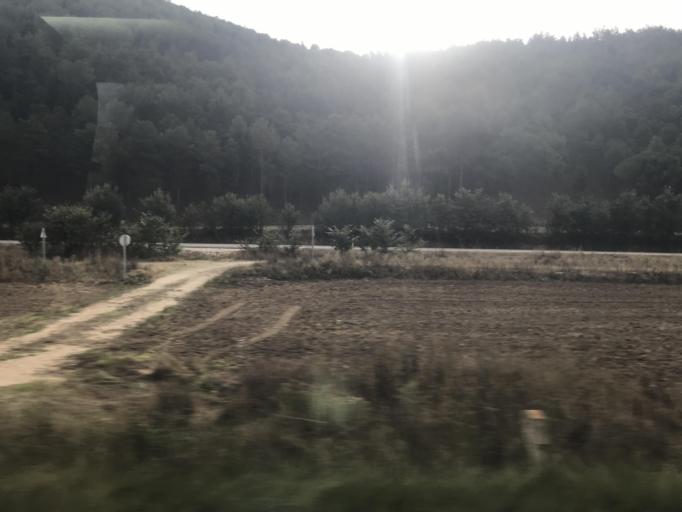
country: ES
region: Castille and Leon
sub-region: Provincia de Burgos
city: Pradanos de Bureba
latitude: 42.5201
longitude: -3.3353
